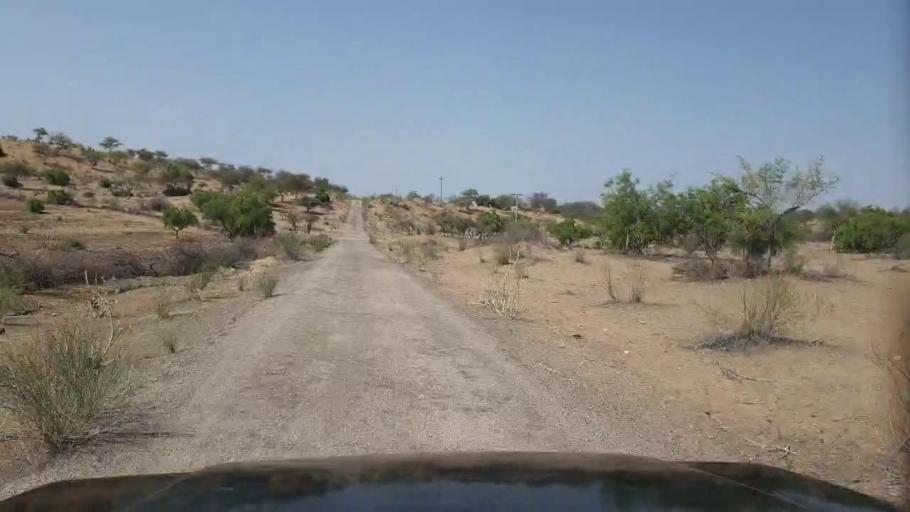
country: PK
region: Sindh
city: Mithi
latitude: 24.9708
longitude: 69.9700
